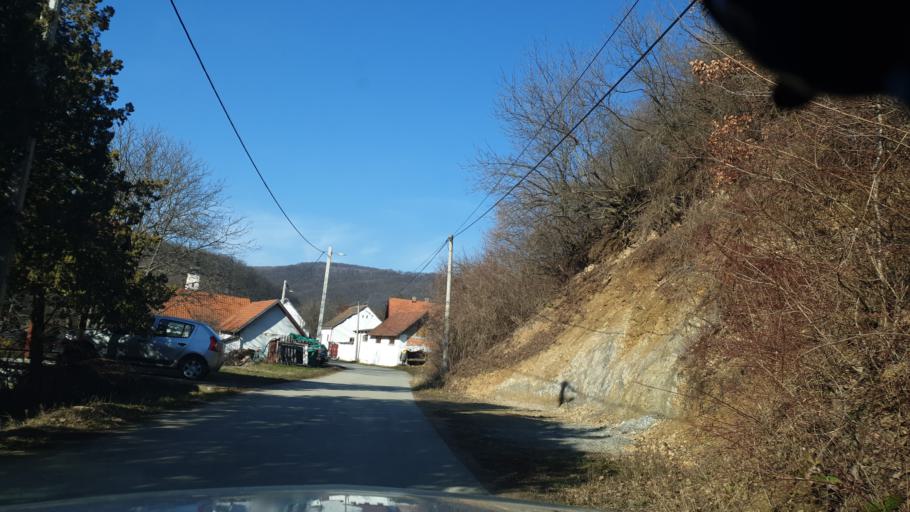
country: RS
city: Vrdnik
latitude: 45.1156
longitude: 19.7667
